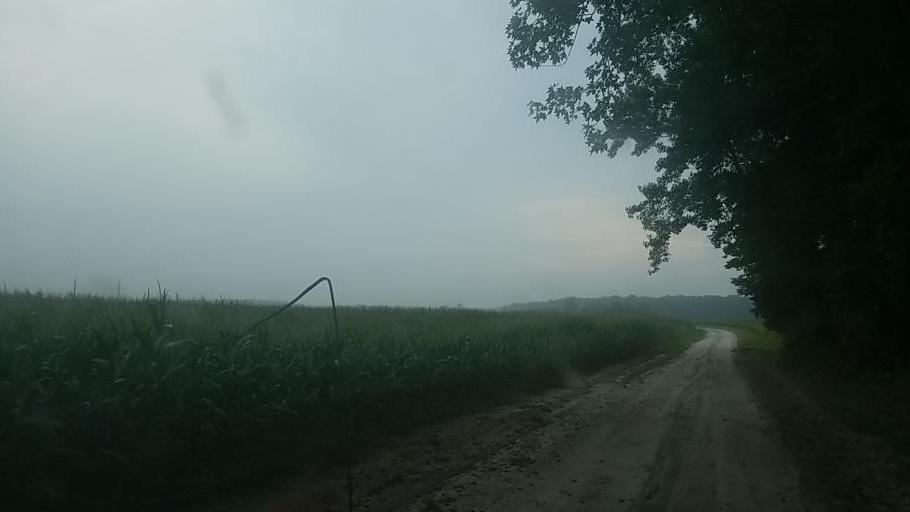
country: US
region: Maryland
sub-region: Wicomico County
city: Pittsville
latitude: 38.4448
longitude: -75.4313
